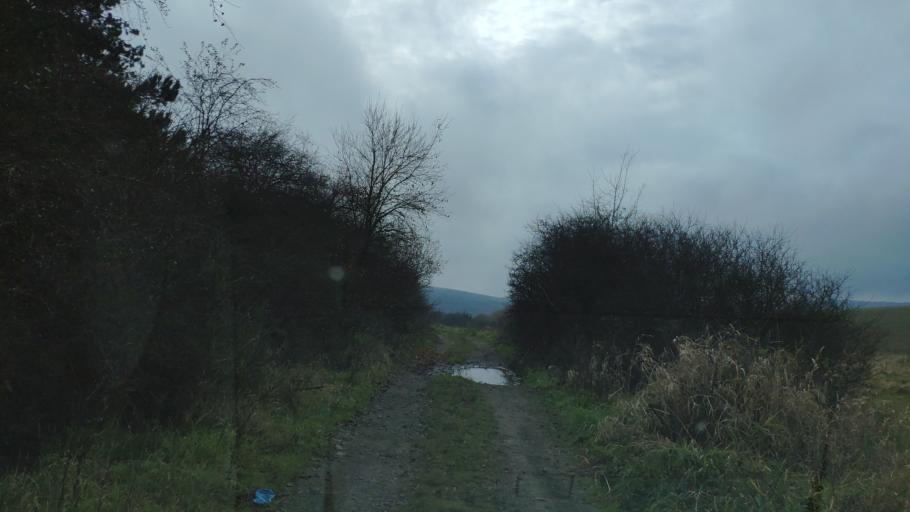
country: SK
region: Presovsky
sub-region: Okres Presov
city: Presov
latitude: 49.0236
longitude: 21.1985
